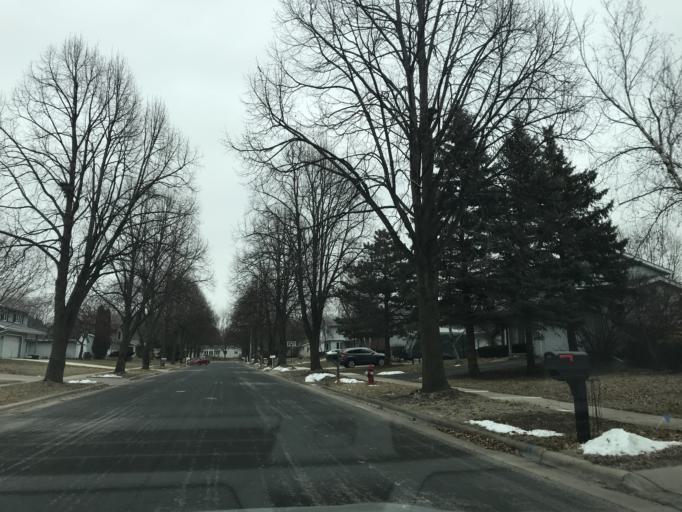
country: US
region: Wisconsin
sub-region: Dane County
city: Monona
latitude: 43.0972
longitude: -89.2945
